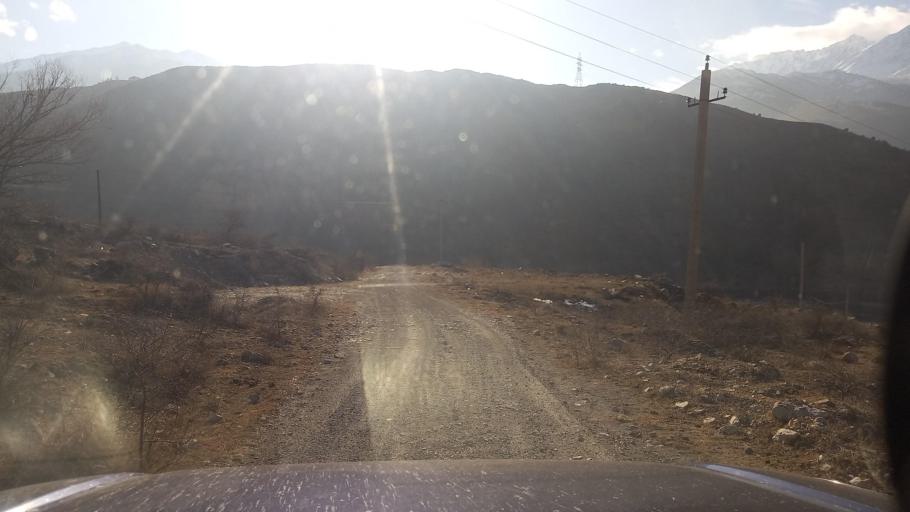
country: RU
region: Ingushetiya
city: Dzhayrakh
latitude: 42.8450
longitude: 44.6513
